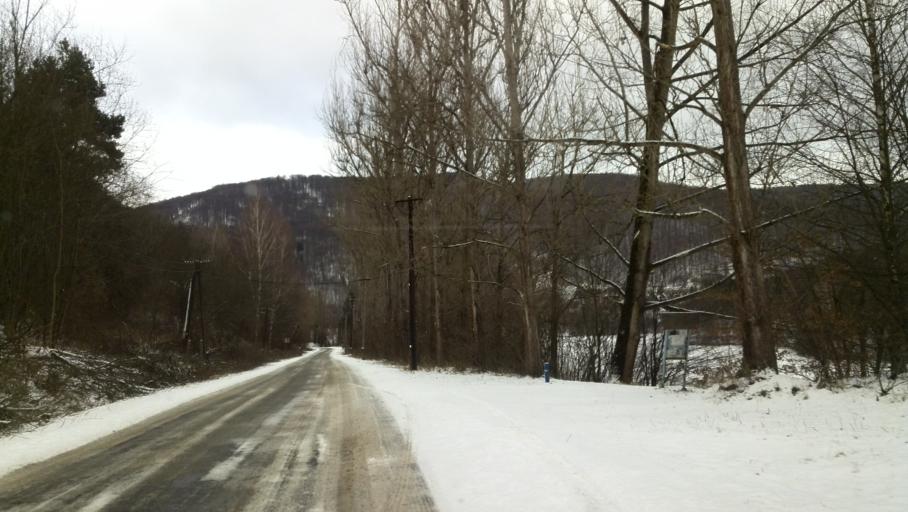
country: SK
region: Kosicky
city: Gelnica
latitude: 48.8280
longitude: 21.0683
